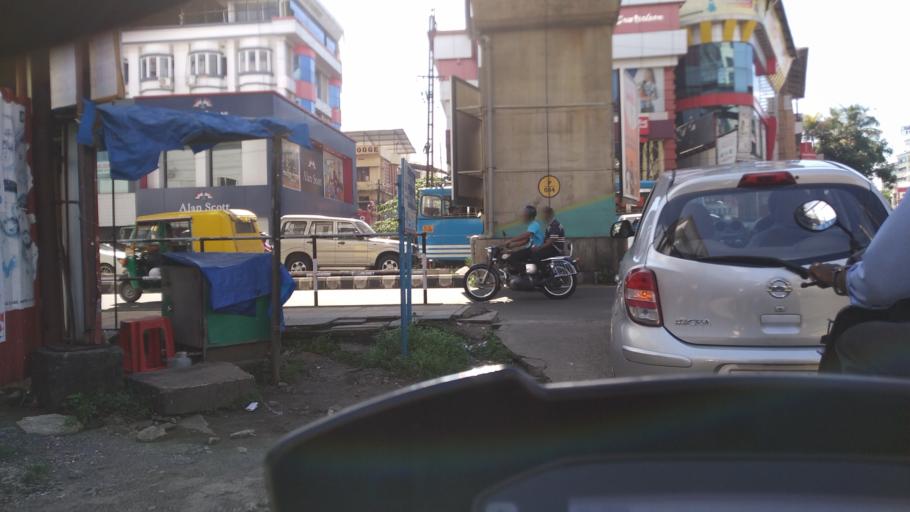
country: IN
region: Kerala
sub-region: Ernakulam
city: Cochin
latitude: 9.9765
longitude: 76.2850
